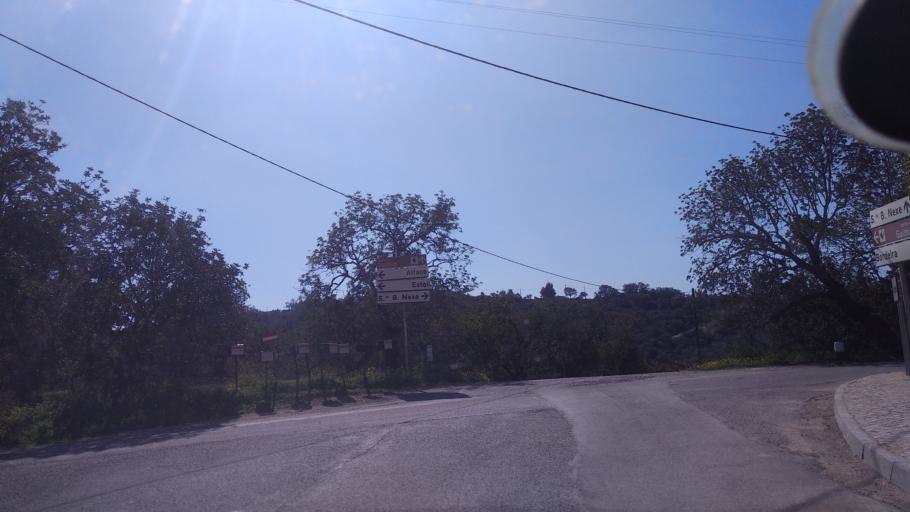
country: PT
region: Faro
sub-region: Faro
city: Santa Barbara de Nexe
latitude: 37.1112
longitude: -7.9336
